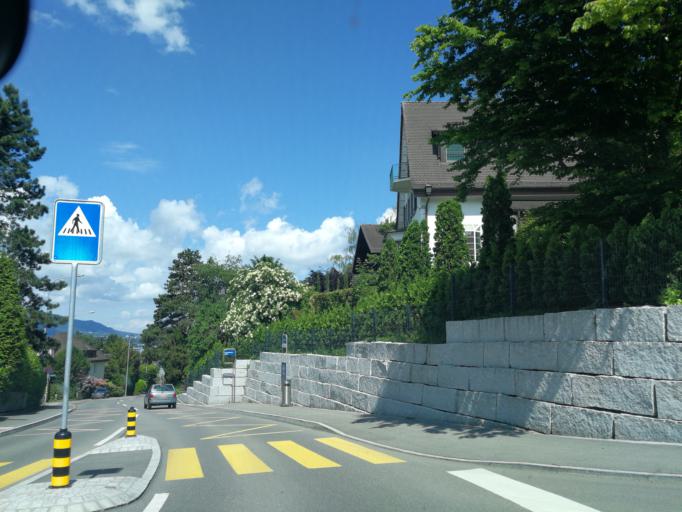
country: CH
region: Zurich
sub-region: Bezirk Meilen
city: Kuesnacht / Schiedhalden
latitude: 47.3215
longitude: 8.5867
